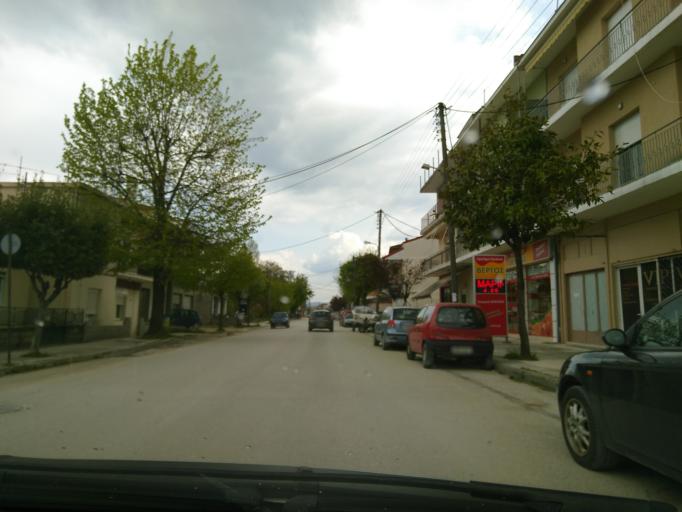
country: GR
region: Epirus
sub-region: Nomos Ioanninon
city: Anatoli
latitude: 39.6449
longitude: 20.8639
